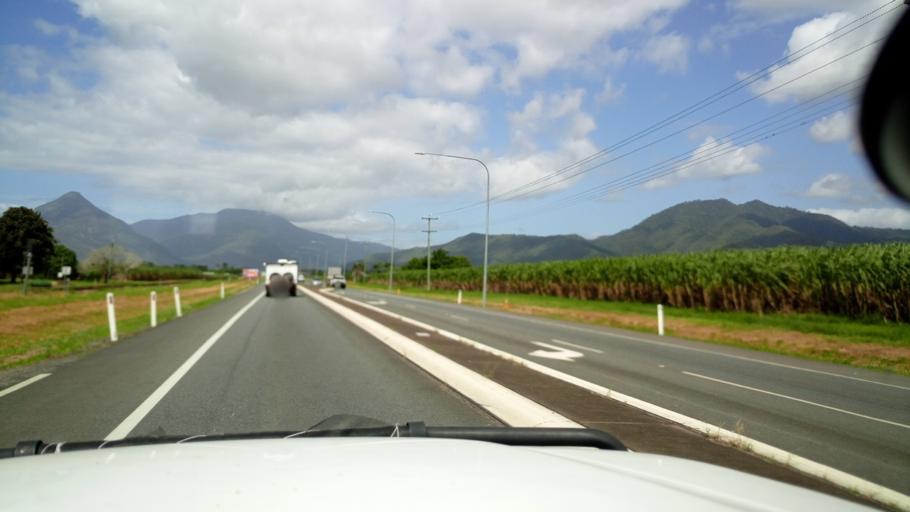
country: AU
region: Queensland
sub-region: Cairns
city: Woree
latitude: -17.0514
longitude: 145.7685
